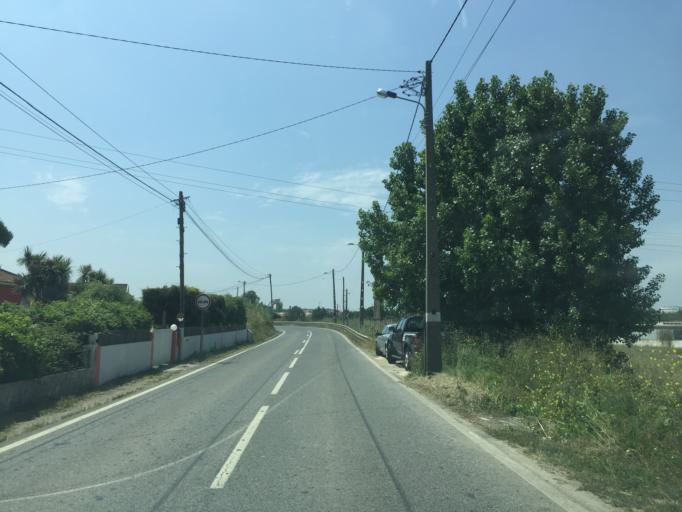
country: PT
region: Lisbon
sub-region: Mafra
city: Venda do Pinheiro
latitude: 38.8912
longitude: -9.1888
